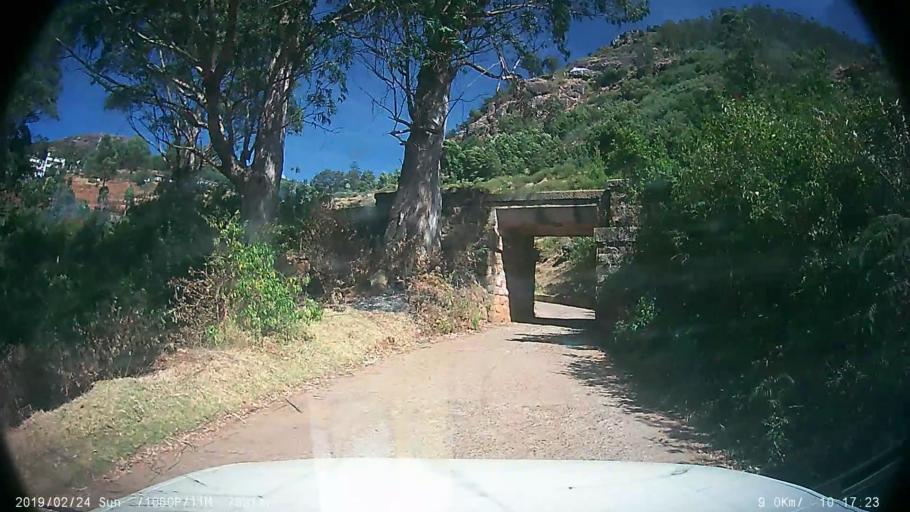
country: IN
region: Tamil Nadu
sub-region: Nilgiri
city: Ooty
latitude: 11.3866
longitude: 76.7223
